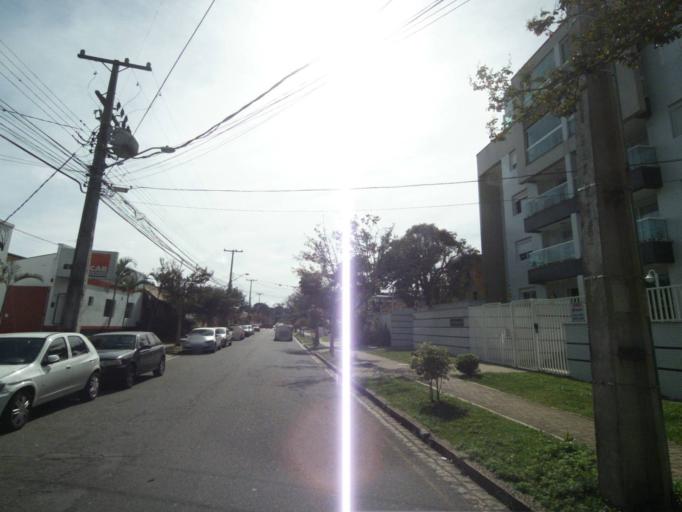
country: BR
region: Parana
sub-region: Curitiba
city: Curitiba
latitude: -25.4233
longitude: -49.2521
